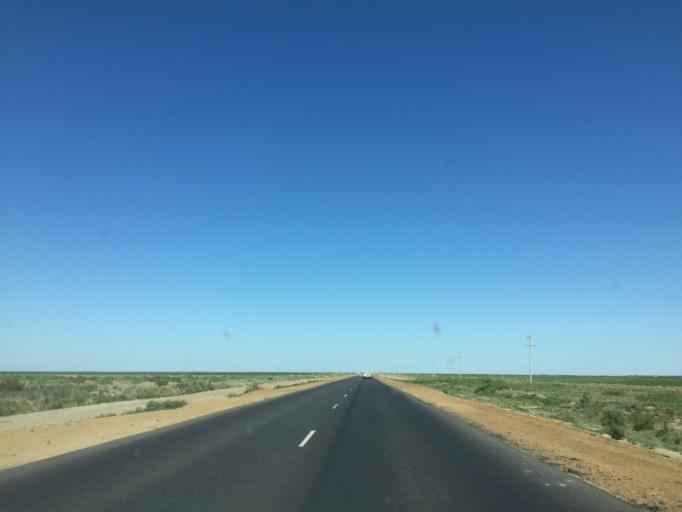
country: KZ
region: Qyzylorda
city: Dzhalagash
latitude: 44.9382
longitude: 64.6402
